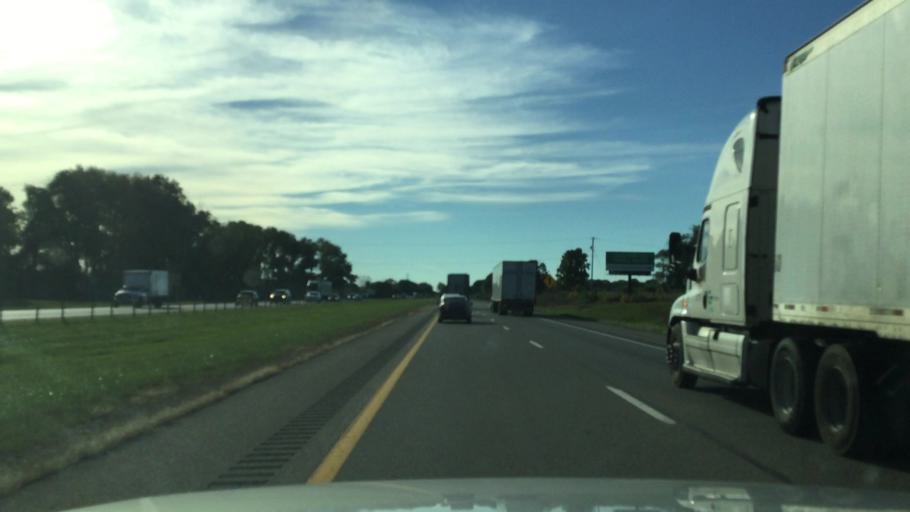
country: US
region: Michigan
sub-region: Calhoun County
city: Lakeview
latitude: 42.2653
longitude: -85.2386
